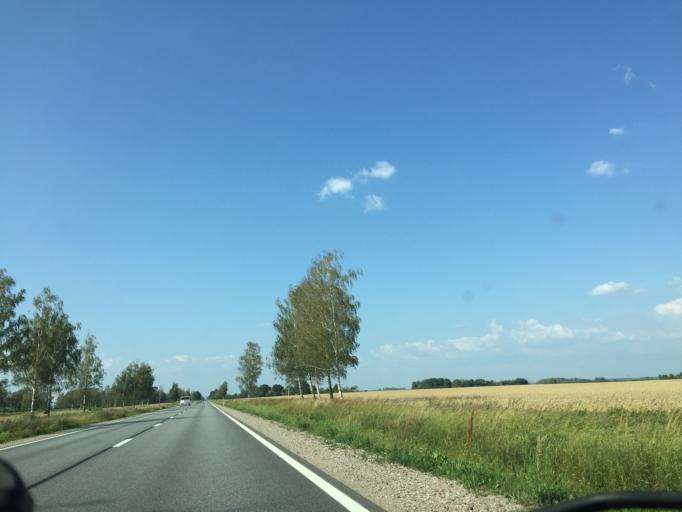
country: LV
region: Jelgava
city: Jelgava
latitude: 56.4733
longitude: 23.6947
